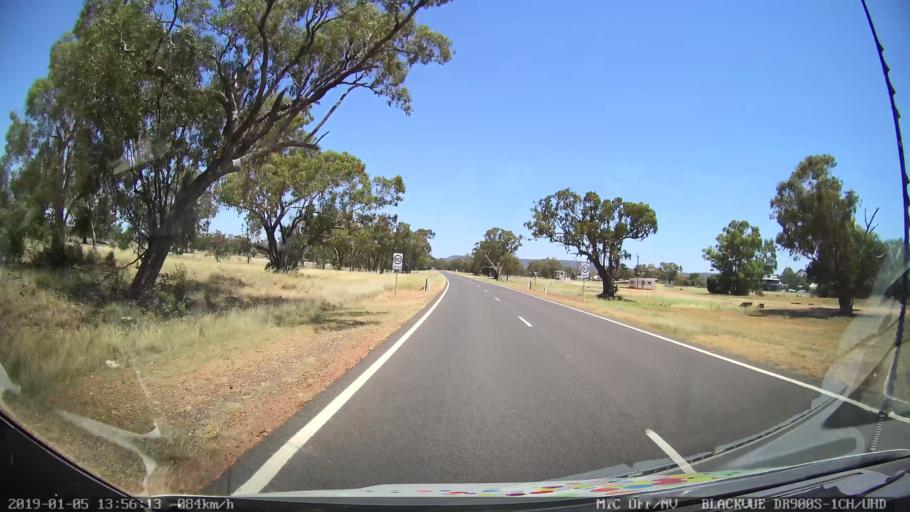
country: AU
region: New South Wales
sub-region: Gunnedah
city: Gunnedah
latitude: -31.1138
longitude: 150.2703
